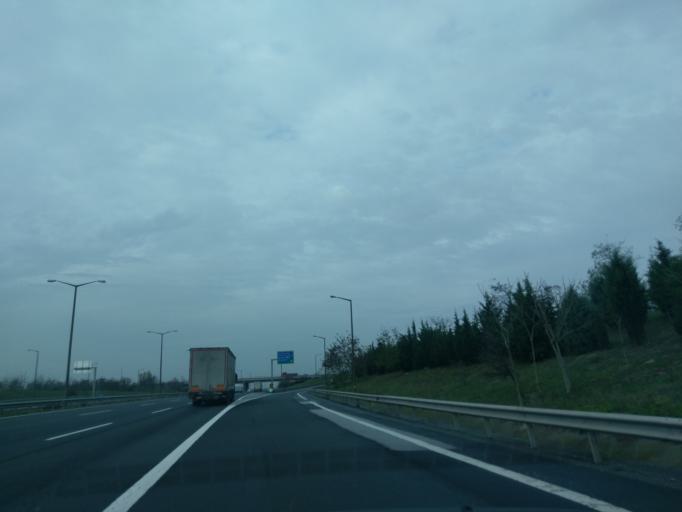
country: TR
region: Istanbul
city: Buyukcavuslu
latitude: 41.1920
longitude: 28.0880
